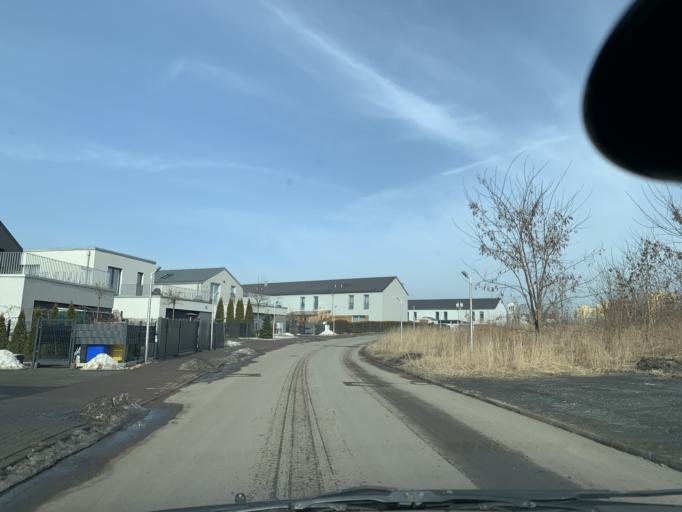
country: PL
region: Silesian Voivodeship
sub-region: Bytom
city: Bytom
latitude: 50.3358
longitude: 18.9050
